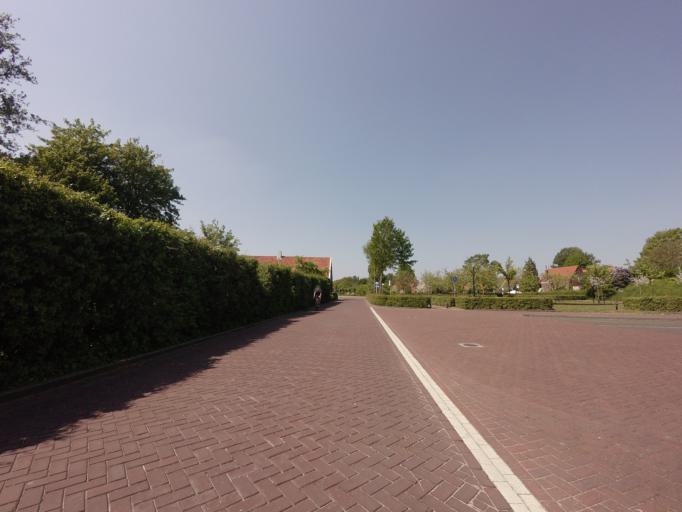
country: NL
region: Zeeland
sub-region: Gemeente Veere
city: Veere
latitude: 51.5454
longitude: 3.6666
